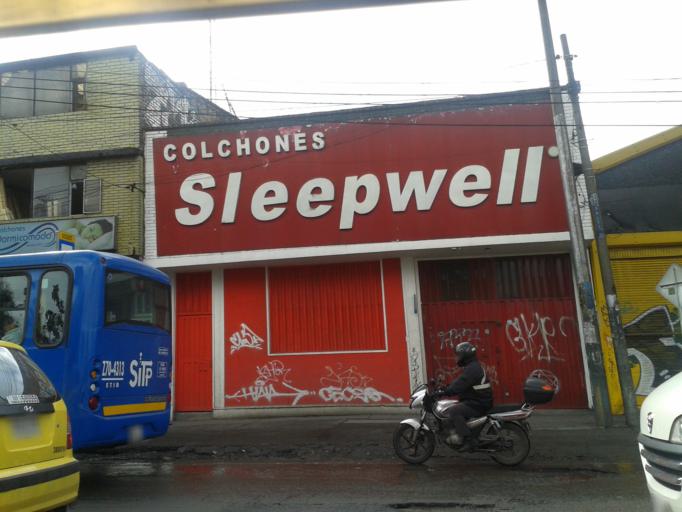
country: CO
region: Bogota D.C.
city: Bogota
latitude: 4.6317
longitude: -74.1213
